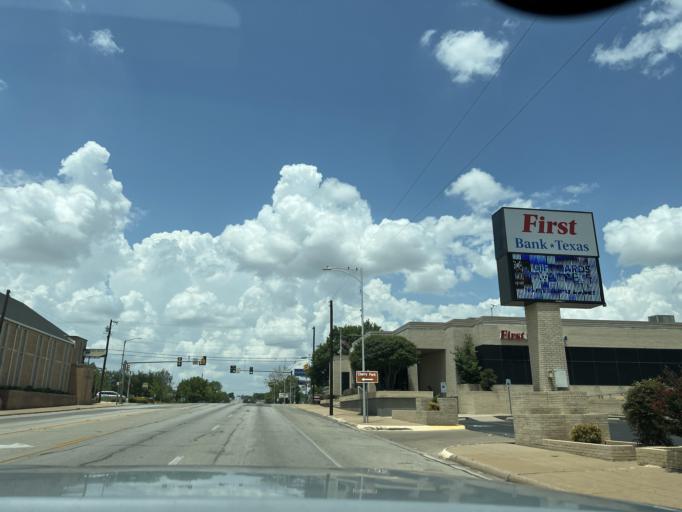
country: US
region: Texas
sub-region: Parker County
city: Weatherford
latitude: 32.7590
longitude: -97.7994
